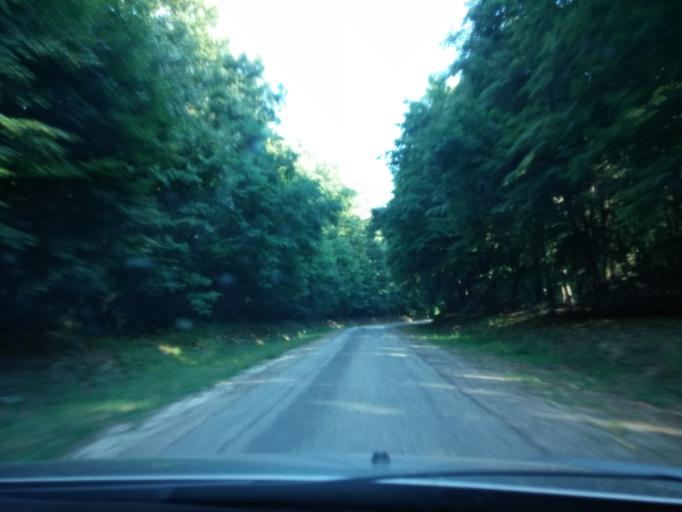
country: HU
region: Somogy
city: Kaposmero
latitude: 46.2477
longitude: 17.7573
